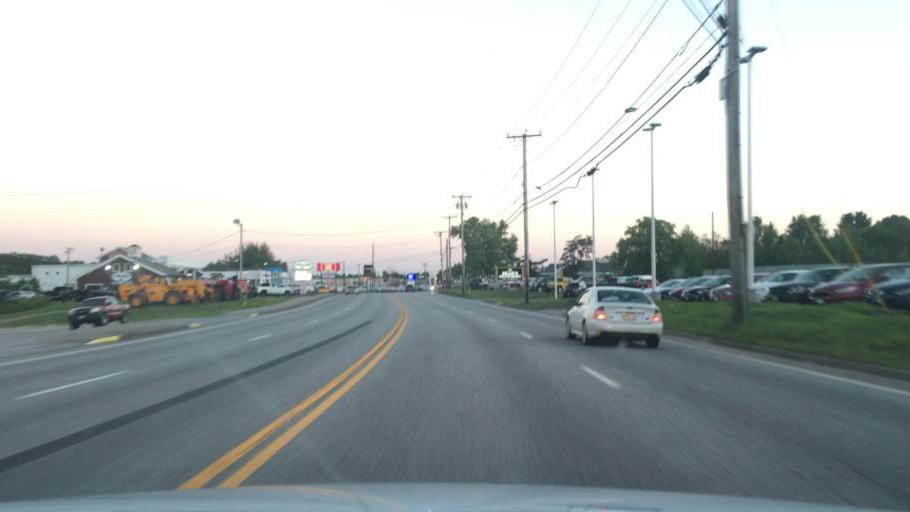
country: US
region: Maine
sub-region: Androscoggin County
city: Lewiston
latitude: 44.1325
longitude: -70.2254
